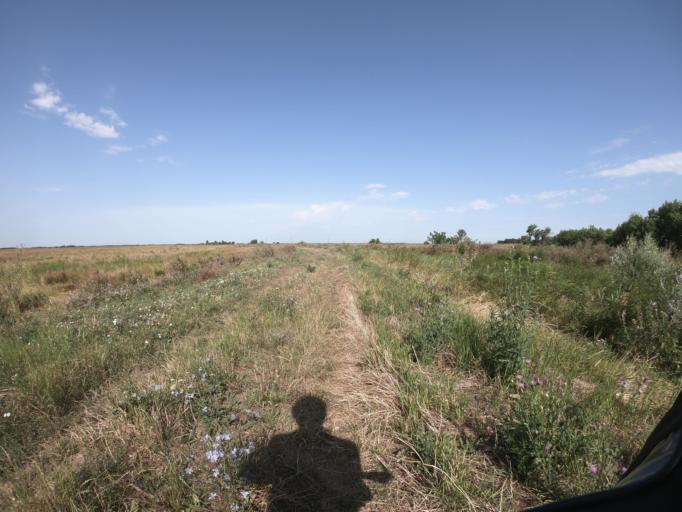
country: HU
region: Hajdu-Bihar
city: Egyek
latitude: 47.5788
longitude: 20.9227
